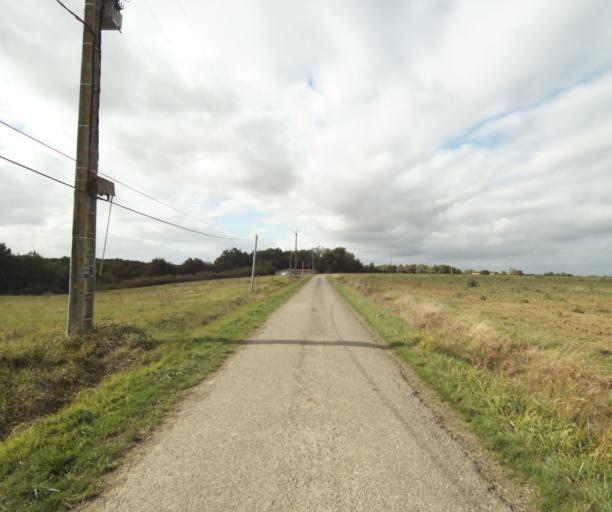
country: FR
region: Midi-Pyrenees
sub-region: Departement du Tarn-et-Garonne
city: Beaumont-de-Lomagne
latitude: 43.8843
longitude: 1.0837
